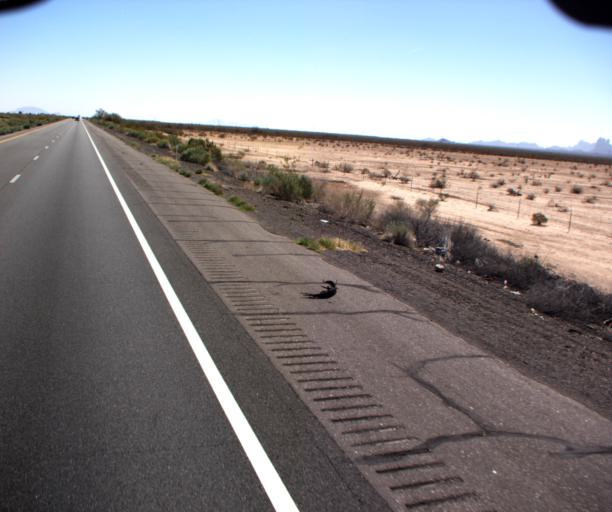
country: US
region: Arizona
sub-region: La Paz County
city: Salome
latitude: 33.5841
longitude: -113.4550
